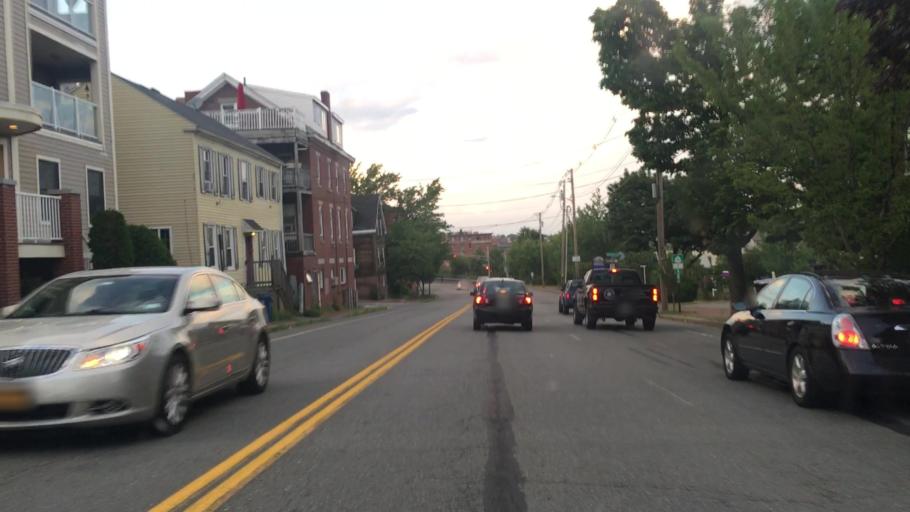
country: US
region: Maine
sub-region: Cumberland County
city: Portland
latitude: 43.6498
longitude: -70.2594
